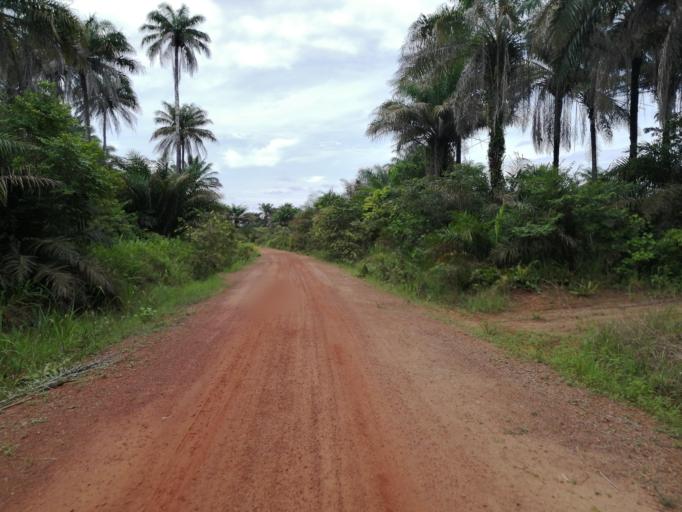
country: SL
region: Northern Province
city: Port Loko
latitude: 8.7781
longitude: -12.9199
